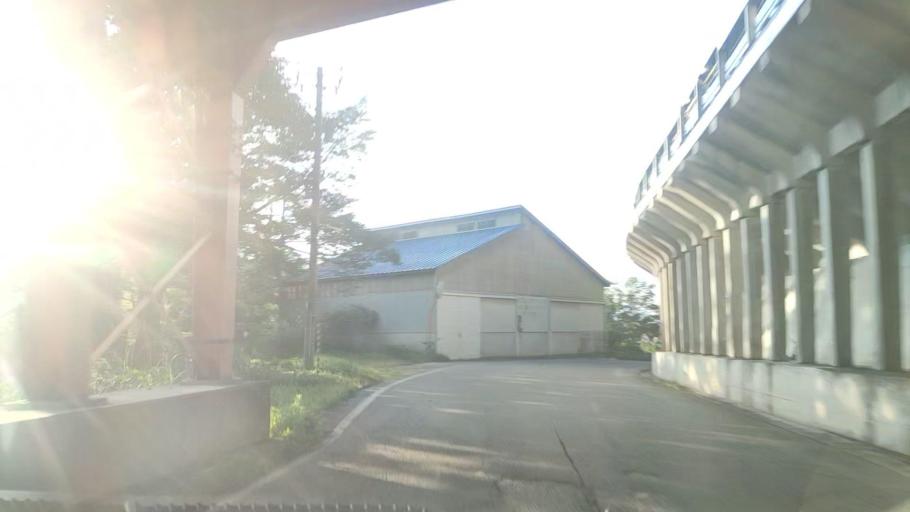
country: JP
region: Toyama
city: Yatsuomachi-higashikumisaka
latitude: 36.4916
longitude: 137.0254
